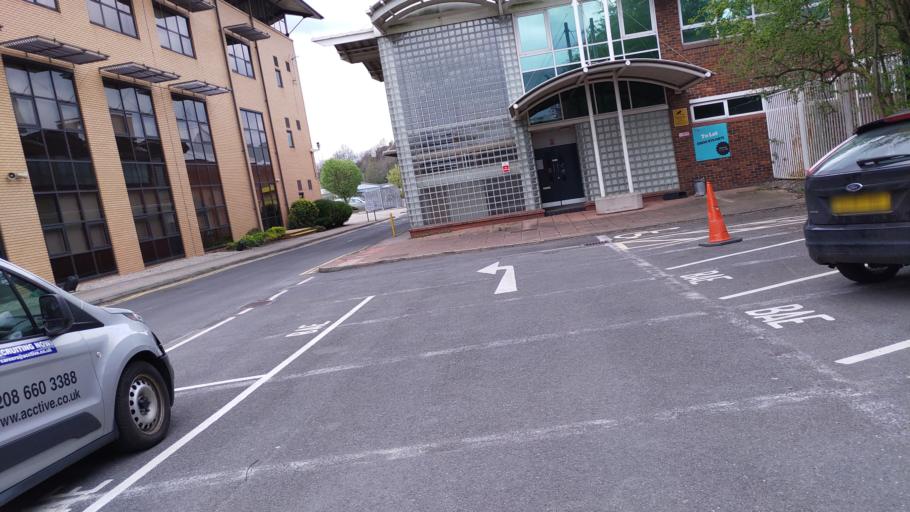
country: GB
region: England
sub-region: Lancashire
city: Preston
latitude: 53.7593
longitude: -2.7175
